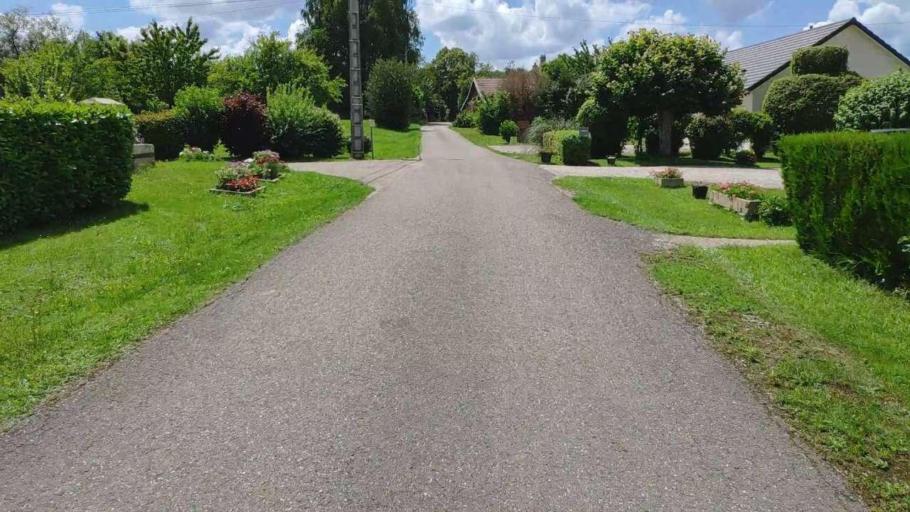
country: FR
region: Franche-Comte
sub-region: Departement du Jura
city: Bletterans
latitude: 46.8414
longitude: 5.4829
